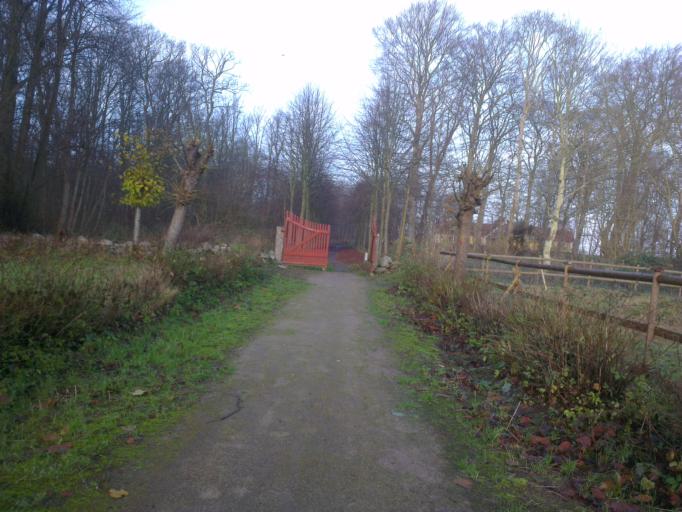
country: DK
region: Capital Region
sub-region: Frederikssund Kommune
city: Jaegerspris
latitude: 55.8629
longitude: 11.9889
